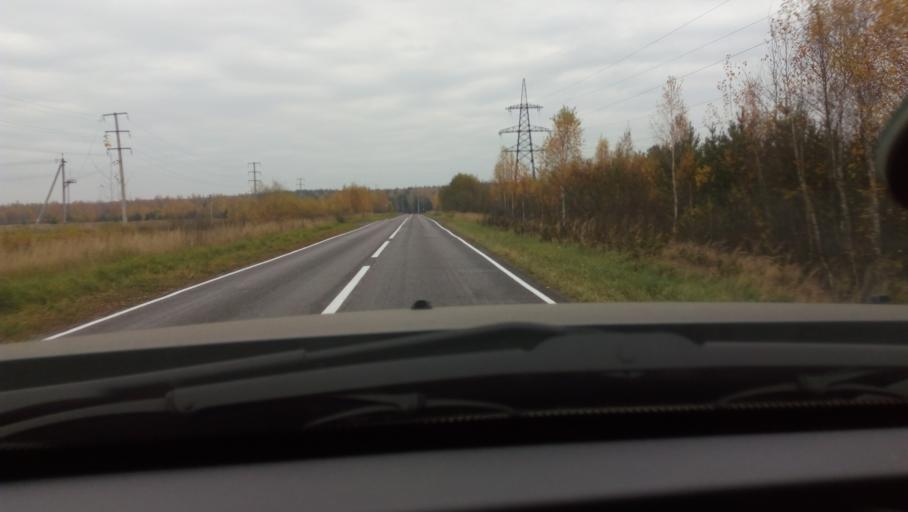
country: RU
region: Moskovskaya
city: Avsyunino
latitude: 55.6042
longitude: 39.1907
